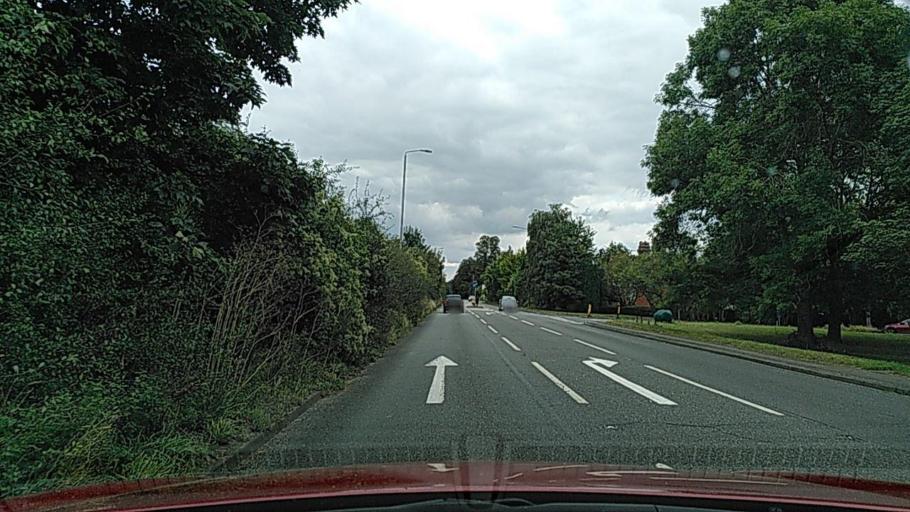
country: GB
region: England
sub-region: Royal Borough of Windsor and Maidenhead
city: White Waltham
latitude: 51.5152
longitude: -0.7953
